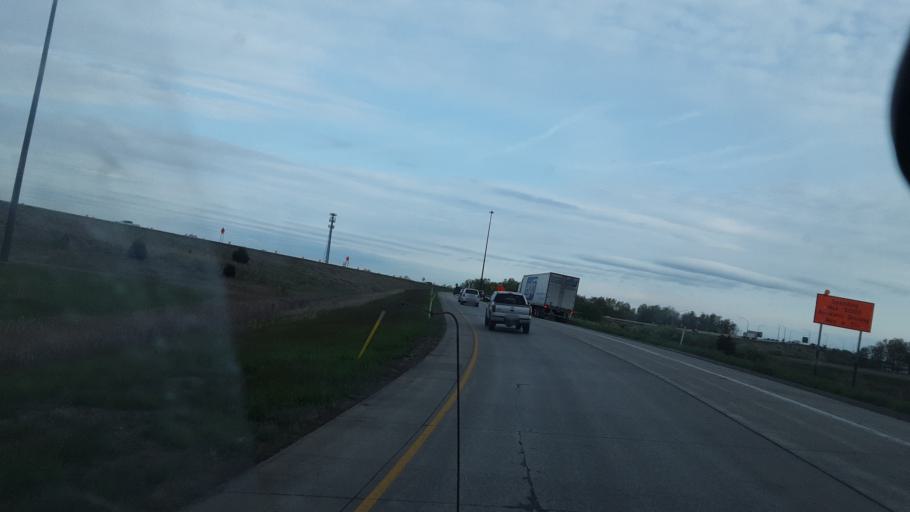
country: US
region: Indiana
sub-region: Allen County
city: New Haven
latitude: 41.0642
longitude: -84.9878
